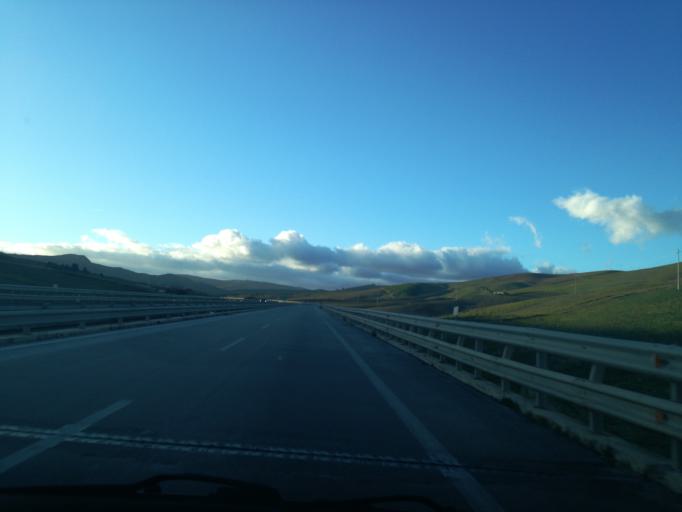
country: IT
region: Sicily
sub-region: Palermo
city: Castellana Sicula
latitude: 37.7419
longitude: 13.9963
